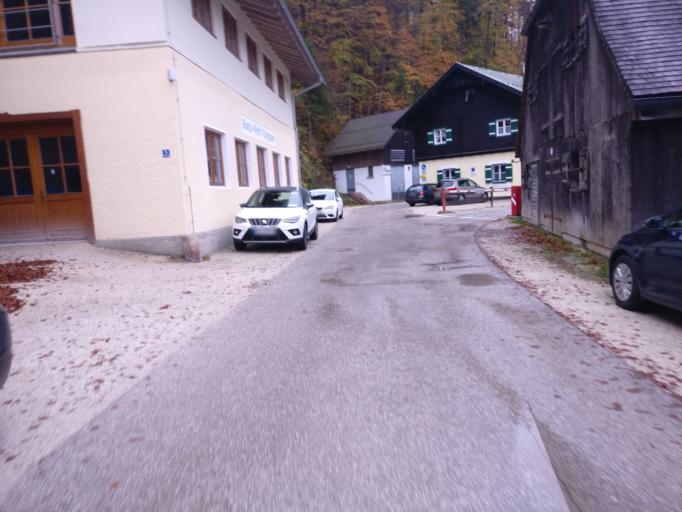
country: DE
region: Bavaria
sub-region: Upper Bavaria
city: Schoenau am Koenigssee
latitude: 47.5875
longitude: 12.9904
